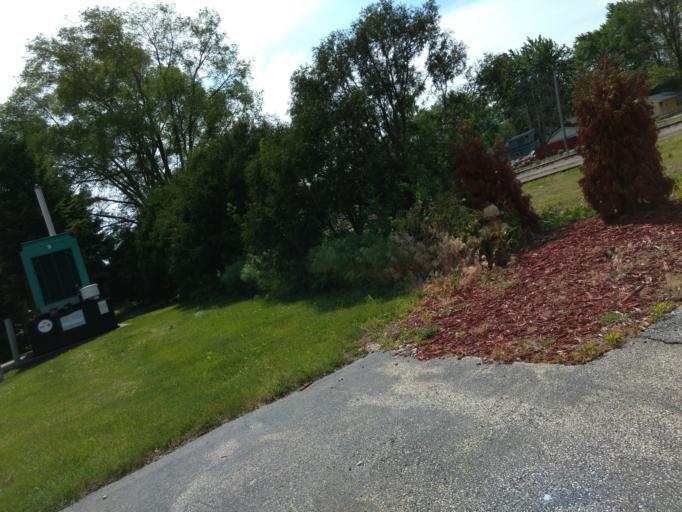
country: US
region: Illinois
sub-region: Champaign County
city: Urbana
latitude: 40.1150
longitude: -88.1958
